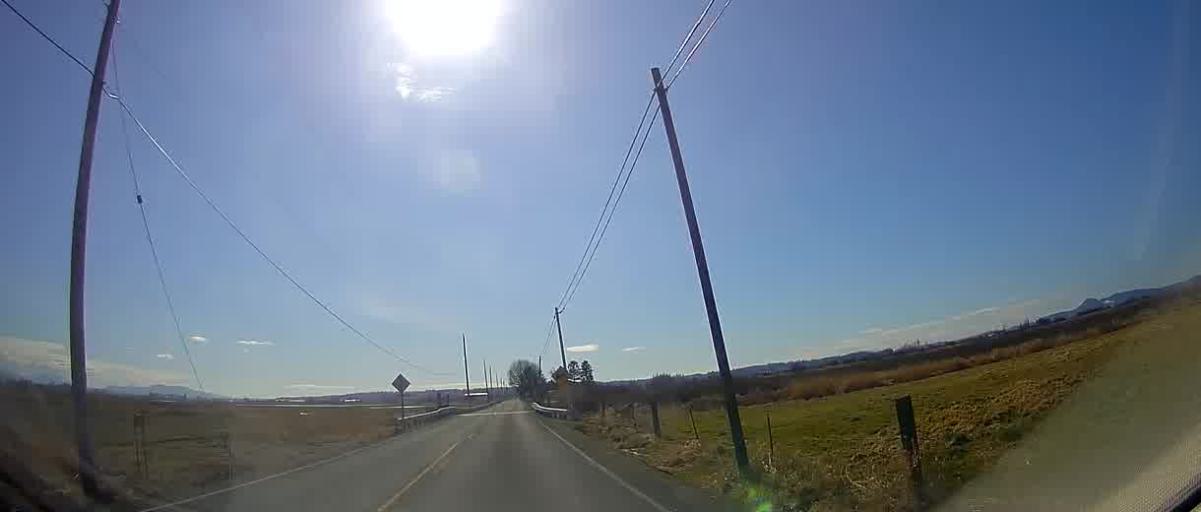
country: US
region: Washington
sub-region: Skagit County
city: Burlington
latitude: 48.5547
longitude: -122.4442
